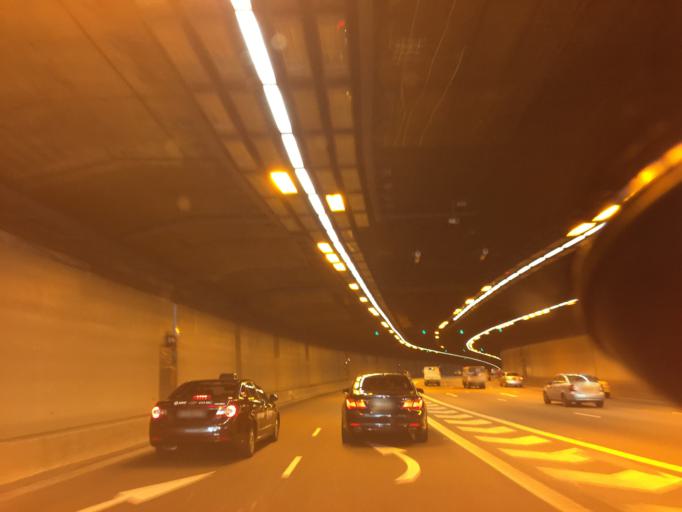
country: SG
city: Singapore
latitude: 1.3071
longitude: 103.8404
